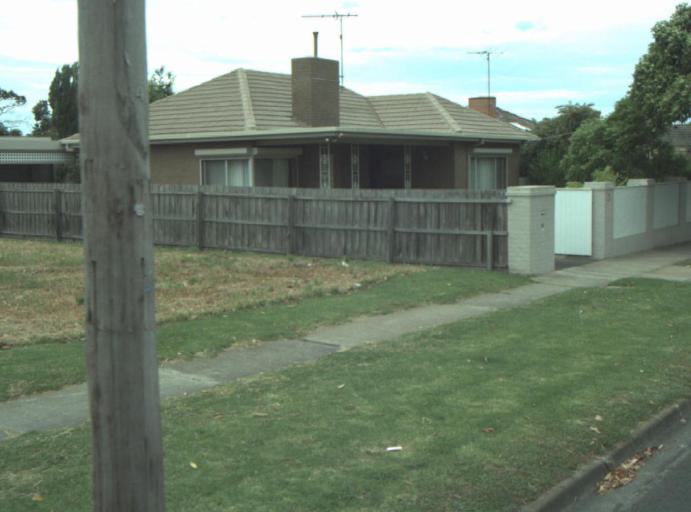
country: AU
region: Victoria
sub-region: Greater Geelong
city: Leopold
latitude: -38.1924
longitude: 144.4684
